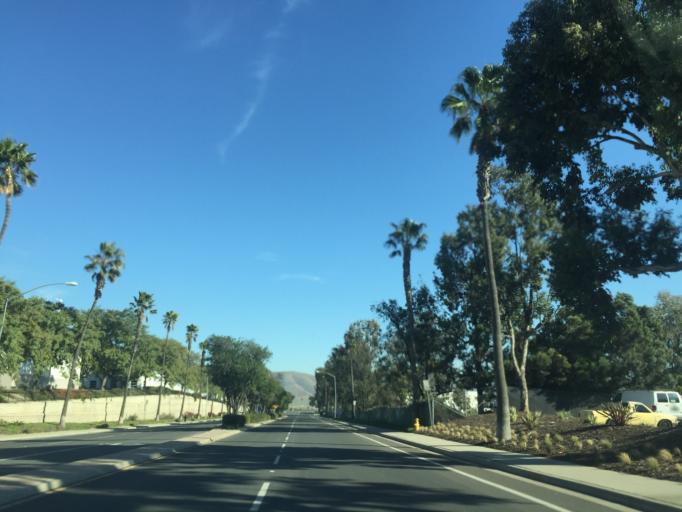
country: MX
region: Baja California
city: Tijuana
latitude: 32.5568
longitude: -116.9315
